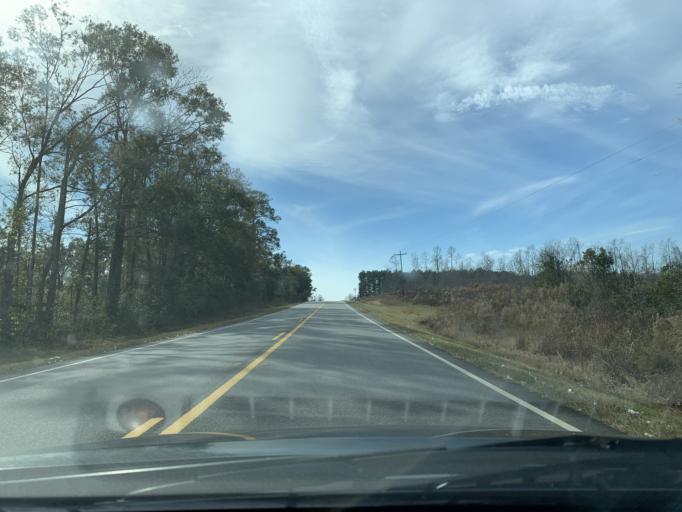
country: US
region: Georgia
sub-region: Turner County
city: Ashburn
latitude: 31.7496
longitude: -83.5605
